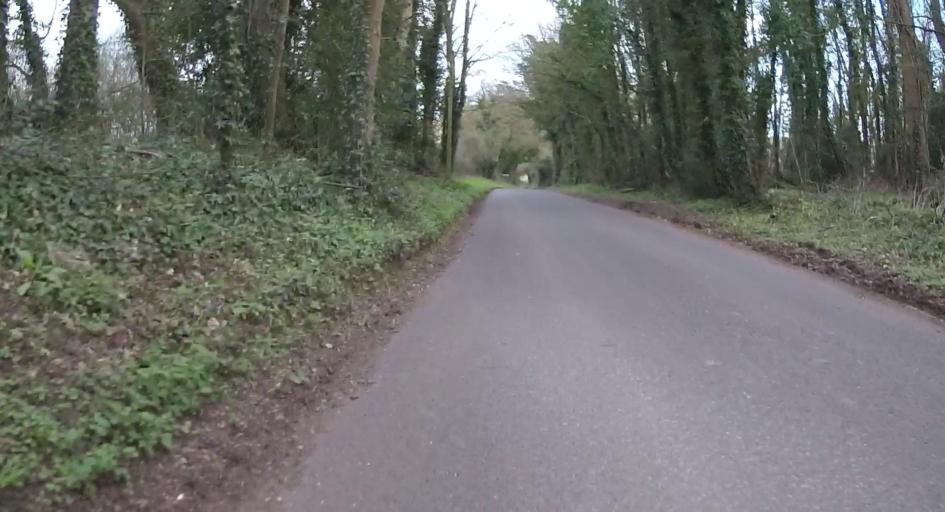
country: GB
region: England
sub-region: Hampshire
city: Andover
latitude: 51.1539
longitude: -1.4660
